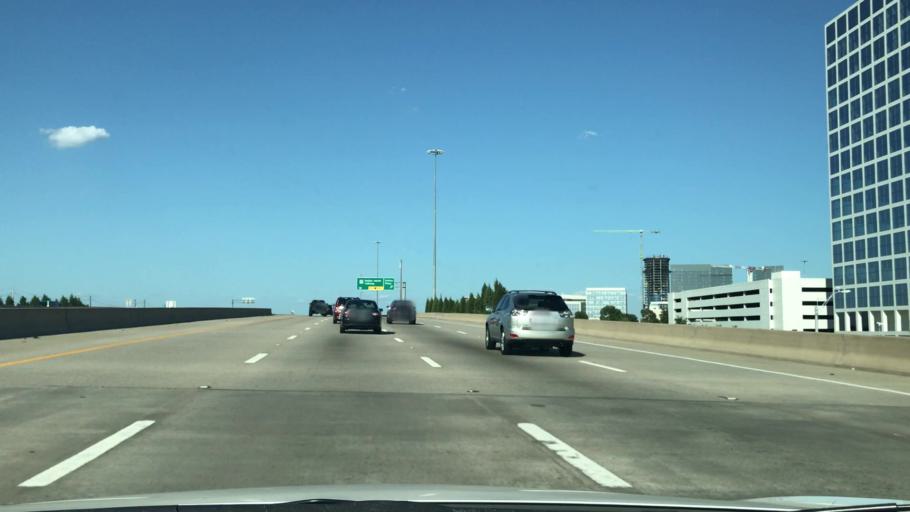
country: US
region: Texas
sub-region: Denton County
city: The Colony
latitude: 33.0863
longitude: -96.8393
